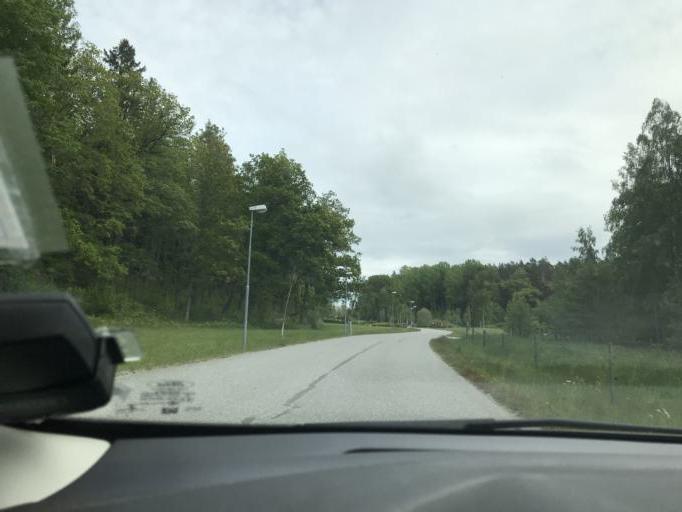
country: SE
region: Stockholm
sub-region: Botkyrka Kommun
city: Alby
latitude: 59.2190
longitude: 17.8441
